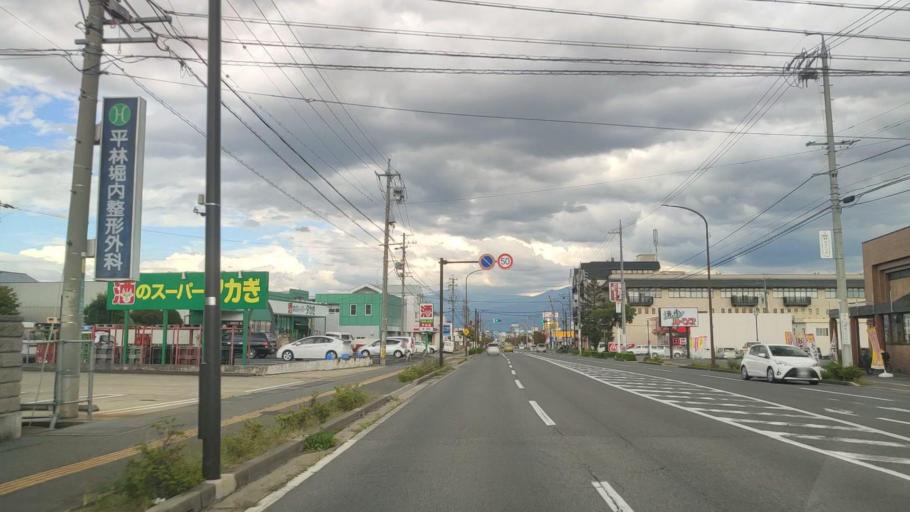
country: JP
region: Nagano
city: Nagano-shi
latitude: 36.6541
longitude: 138.2159
